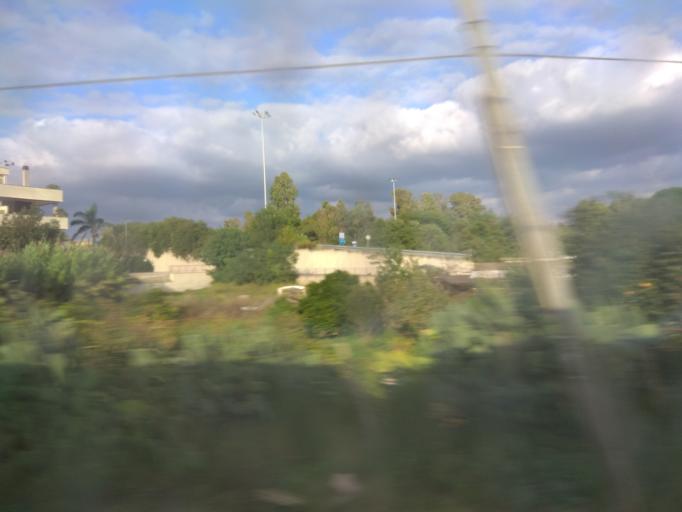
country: IT
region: Latium
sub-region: Citta metropolitana di Roma Capitale
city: Maccarese
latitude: 41.9134
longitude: 12.2021
